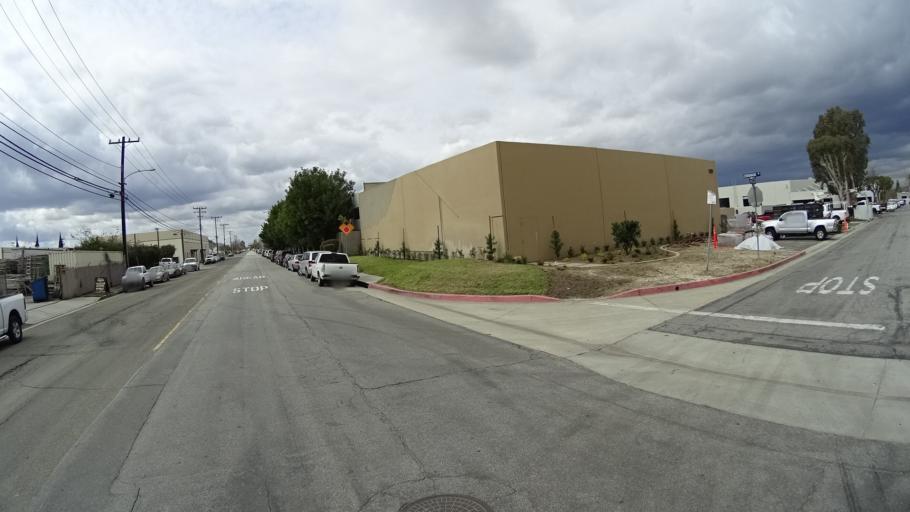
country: US
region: California
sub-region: Orange County
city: Placentia
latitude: 33.8535
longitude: -117.8631
